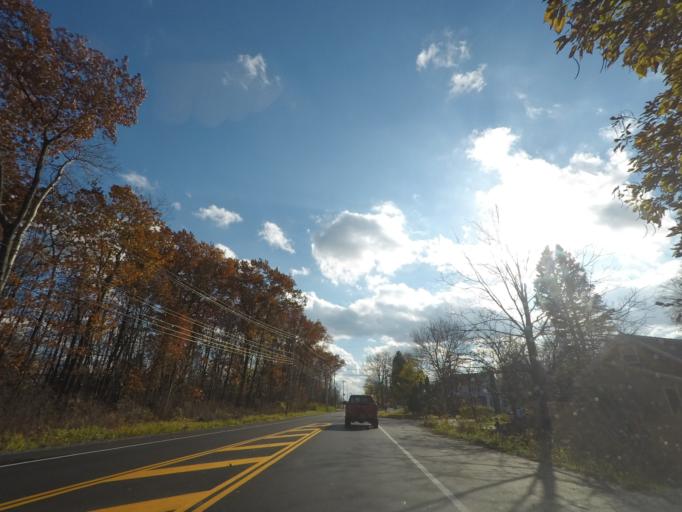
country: US
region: New York
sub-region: Schenectady County
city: Niskayuna
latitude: 42.7814
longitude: -73.8932
